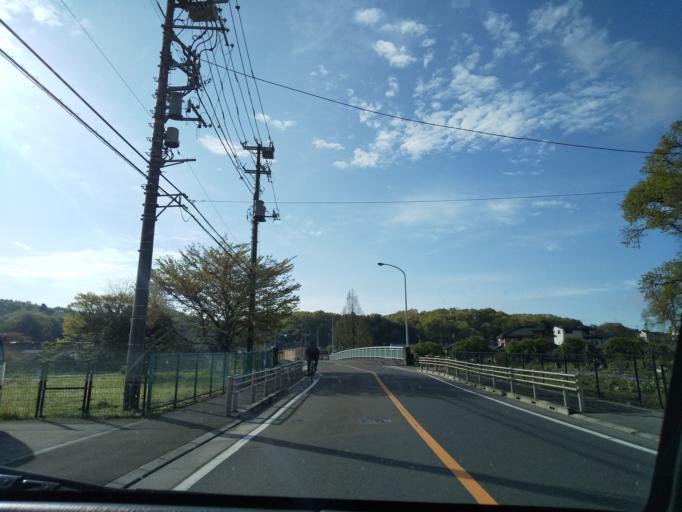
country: JP
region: Tokyo
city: Hachioji
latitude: 35.6793
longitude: 139.2687
